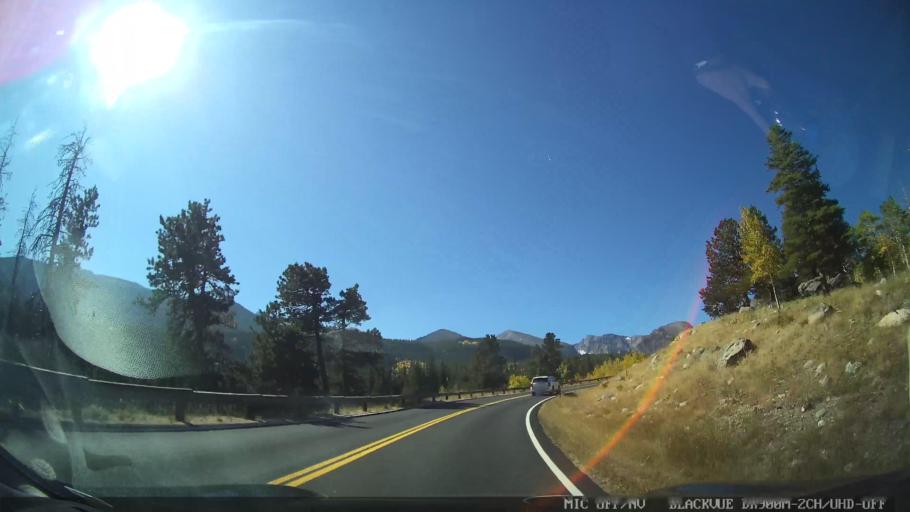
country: US
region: Colorado
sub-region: Larimer County
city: Estes Park
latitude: 40.3215
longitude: -105.6097
